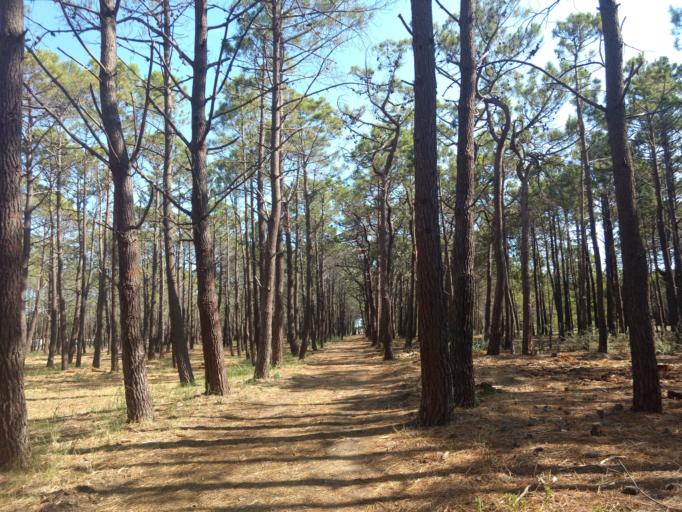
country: FR
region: Languedoc-Roussillon
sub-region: Departement des Pyrenees-Orientales
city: Le Barcares
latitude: 42.8181
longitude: 3.0339
